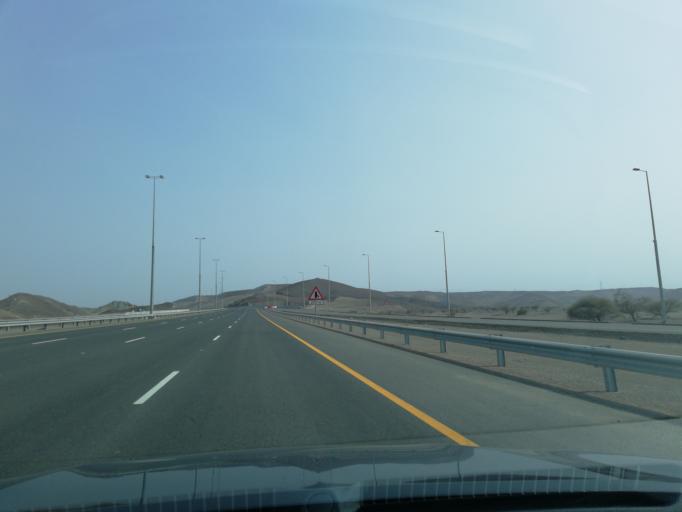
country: OM
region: Al Batinah
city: Al Liwa'
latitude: 24.3599
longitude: 56.5508
